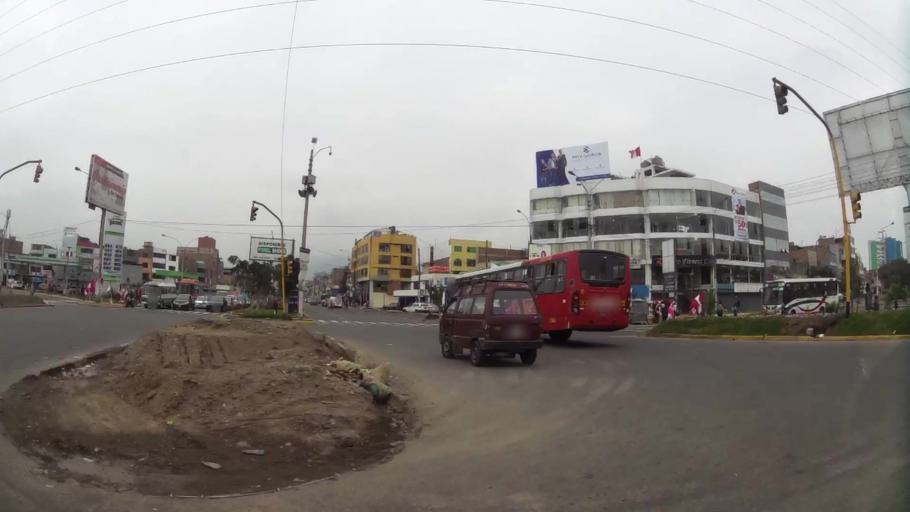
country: PE
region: Lima
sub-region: Lima
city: Independencia
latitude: -11.9962
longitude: -77.0847
